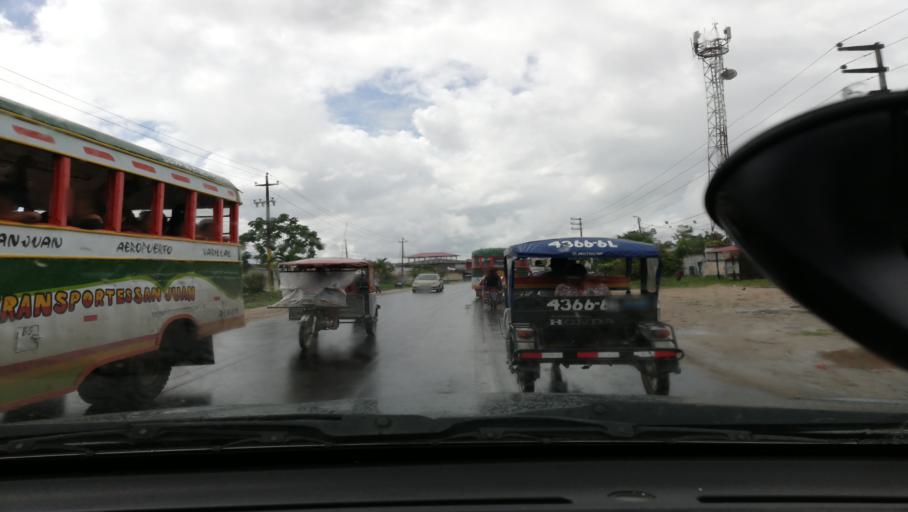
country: PE
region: Loreto
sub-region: Provincia de Maynas
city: Iquitos
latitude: -3.7970
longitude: -73.3034
